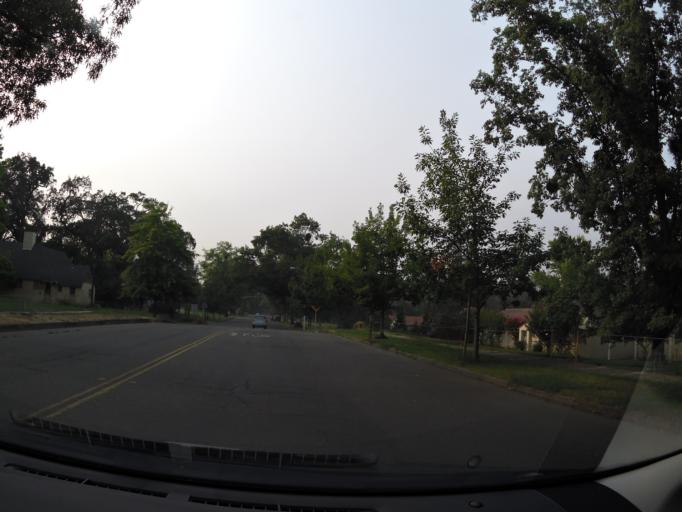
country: US
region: California
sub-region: Sonoma County
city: Eldridge
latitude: 38.3475
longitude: -122.5153
